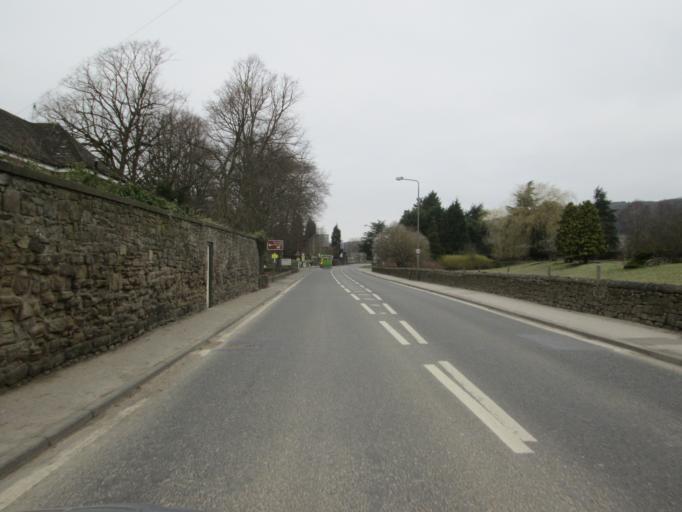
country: GB
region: England
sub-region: Derbyshire
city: Matlock
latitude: 53.1566
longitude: -1.5837
